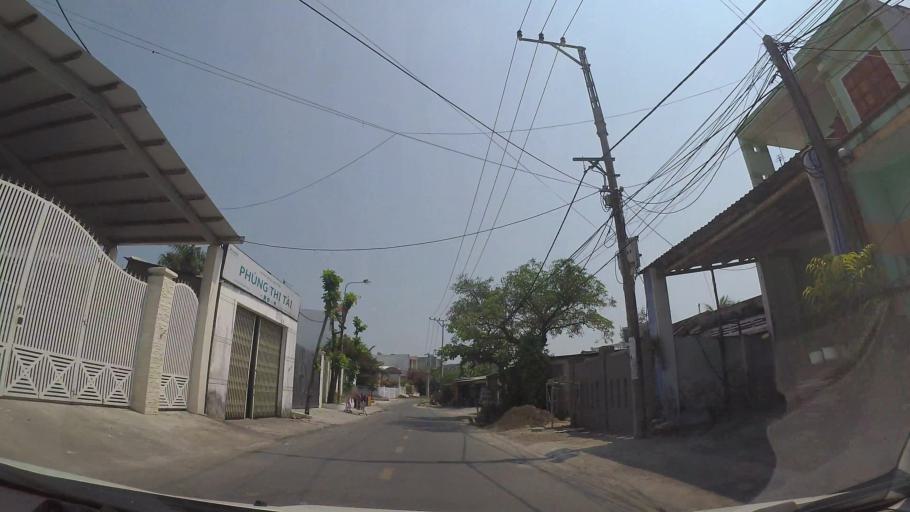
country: VN
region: Da Nang
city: Ngu Hanh Son
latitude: 16.0026
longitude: 108.2659
